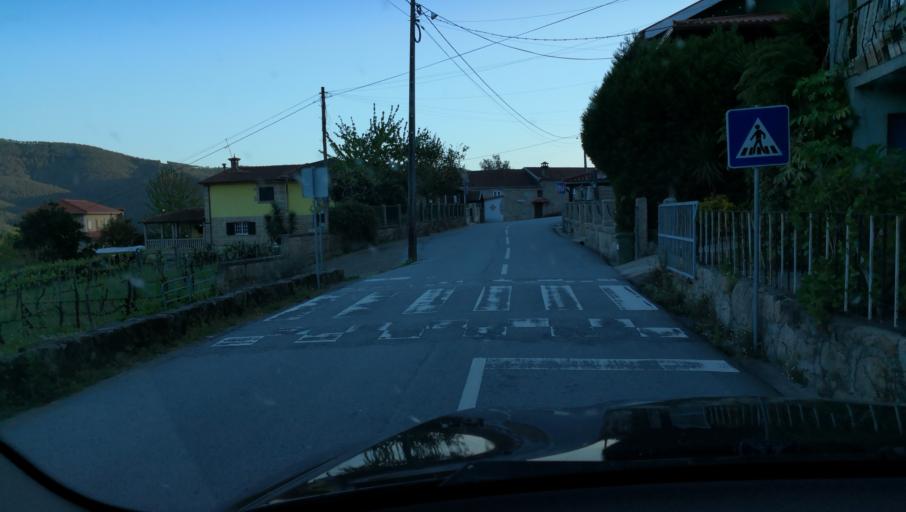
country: PT
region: Vila Real
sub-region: Mondim de Basto
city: Mondim de Basto
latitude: 41.4076
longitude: -7.9057
